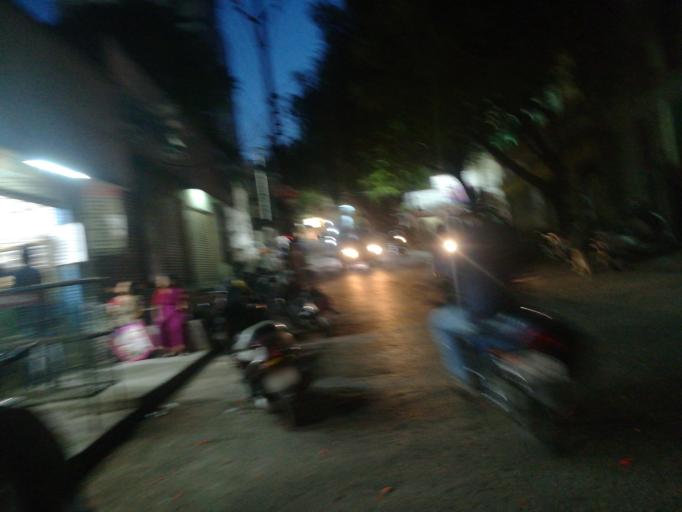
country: IN
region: Telangana
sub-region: Hyderabad
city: Malkajgiri
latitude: 17.4232
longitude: 78.5120
